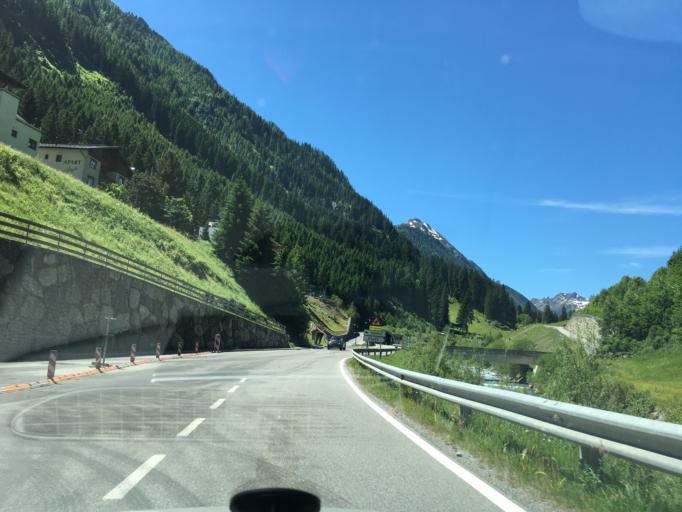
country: AT
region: Tyrol
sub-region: Politischer Bezirk Landeck
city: Ischgl
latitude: 47.0293
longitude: 10.3156
